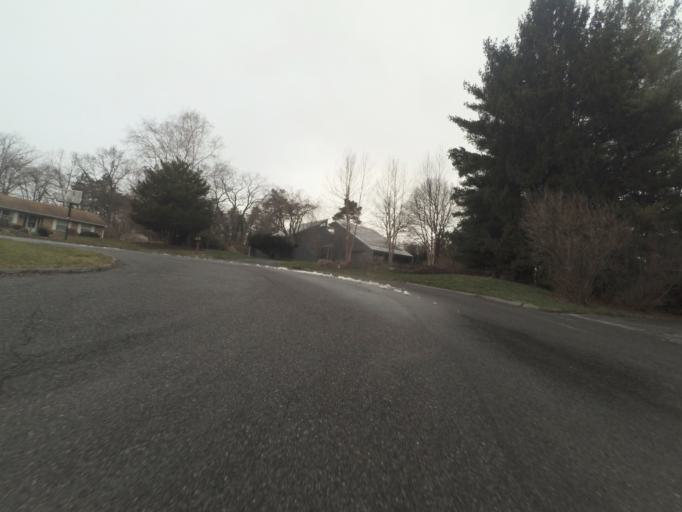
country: US
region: Pennsylvania
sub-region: Centre County
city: State College
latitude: 40.7993
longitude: -77.8438
